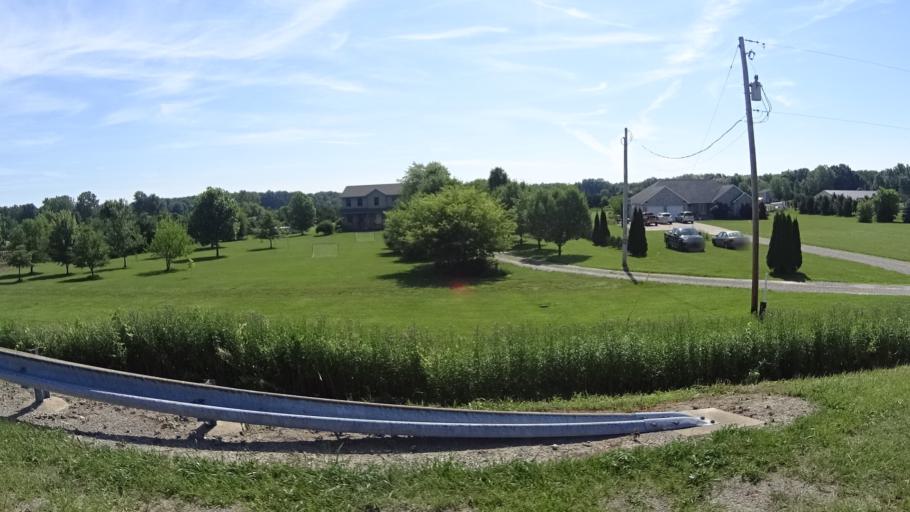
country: US
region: Ohio
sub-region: Erie County
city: Huron
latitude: 41.3664
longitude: -82.4717
